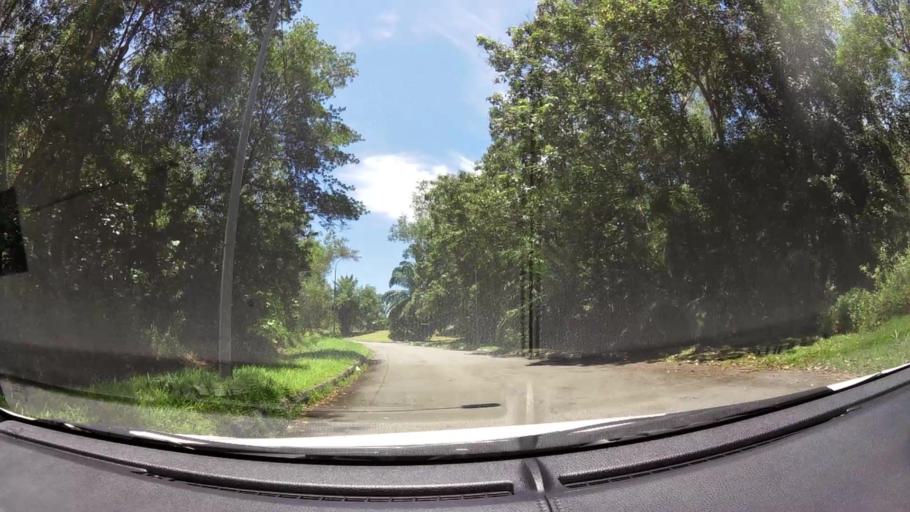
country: BN
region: Brunei and Muara
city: Bandar Seri Begawan
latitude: 4.9195
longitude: 114.9583
